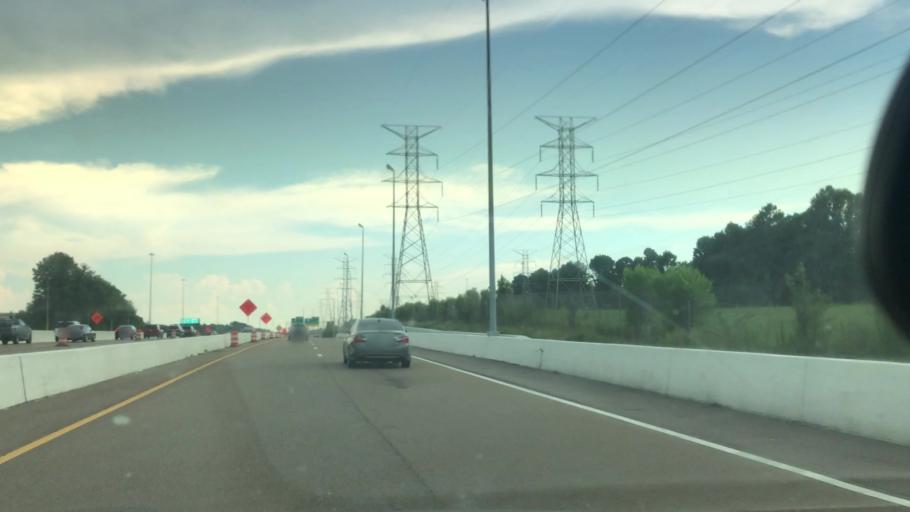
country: US
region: Tennessee
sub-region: Shelby County
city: Germantown
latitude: 35.1090
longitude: -89.8703
